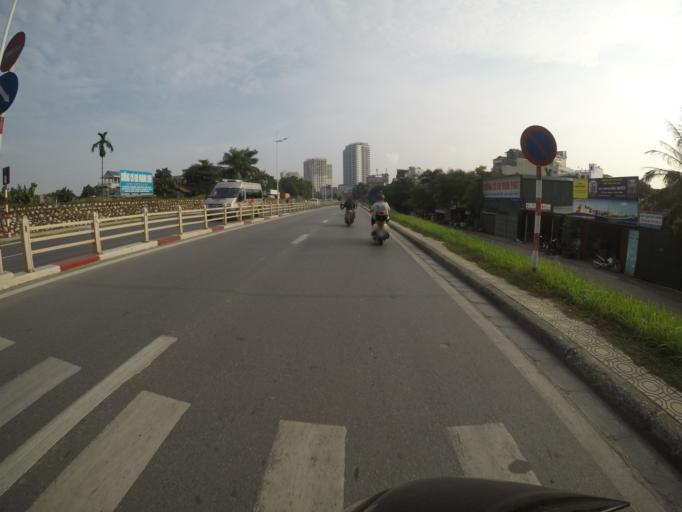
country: VN
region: Ha Noi
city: Tay Ho
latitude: 21.0709
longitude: 105.8260
